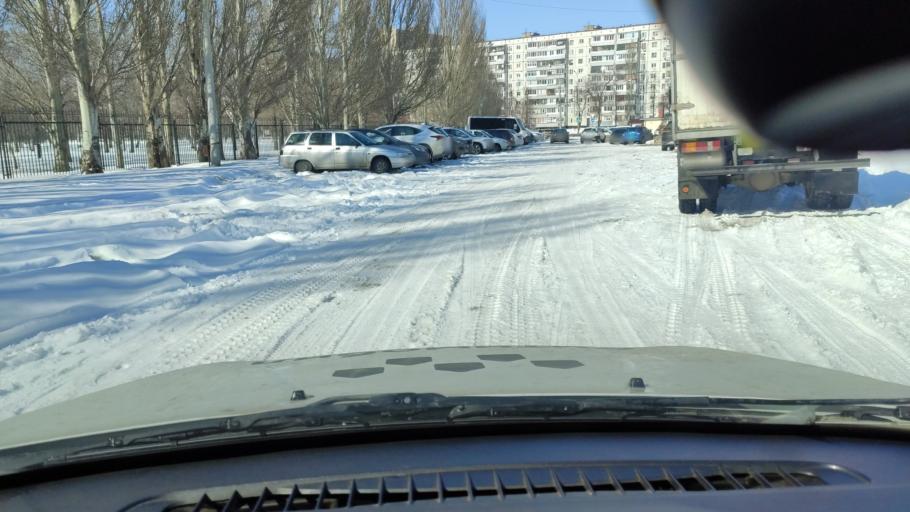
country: RU
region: Samara
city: Tol'yatti
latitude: 53.5065
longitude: 49.2643
